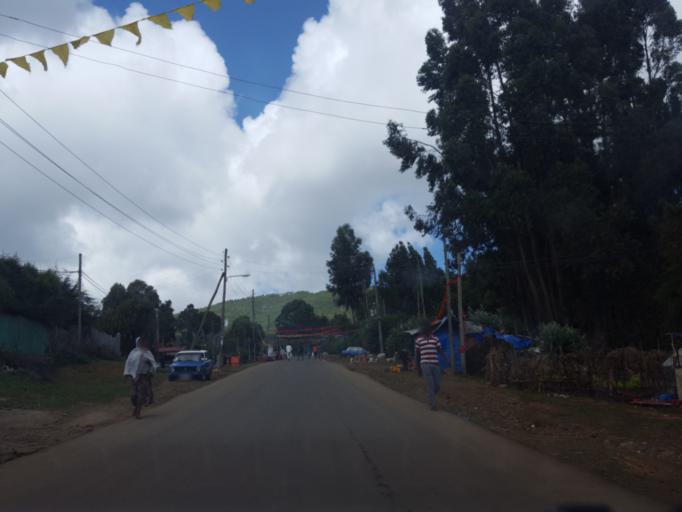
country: ET
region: Adis Abeba
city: Addis Ababa
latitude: 9.0761
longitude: 38.7590
